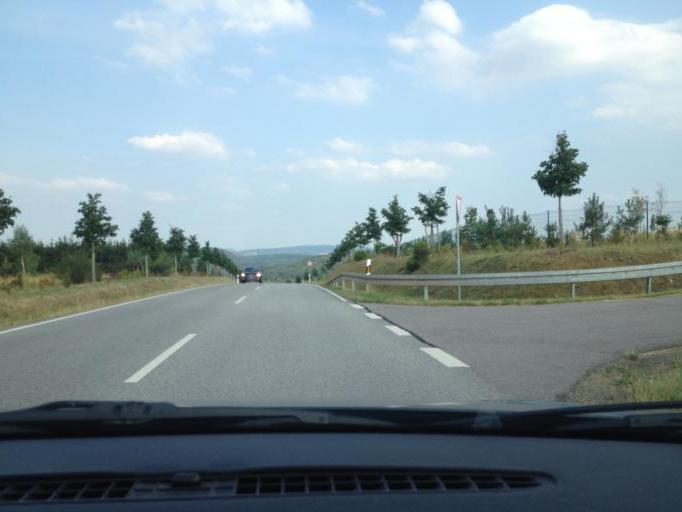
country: DE
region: Rheinland-Pfalz
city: Achtelsbach
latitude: 49.5763
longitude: 7.0784
